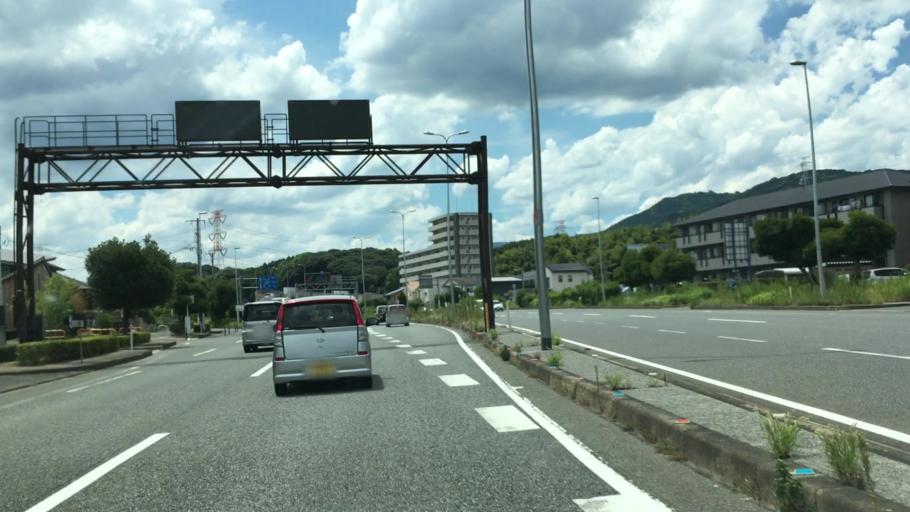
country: JP
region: Fukuoka
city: Chikushino-shi
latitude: 33.4464
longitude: 130.5399
